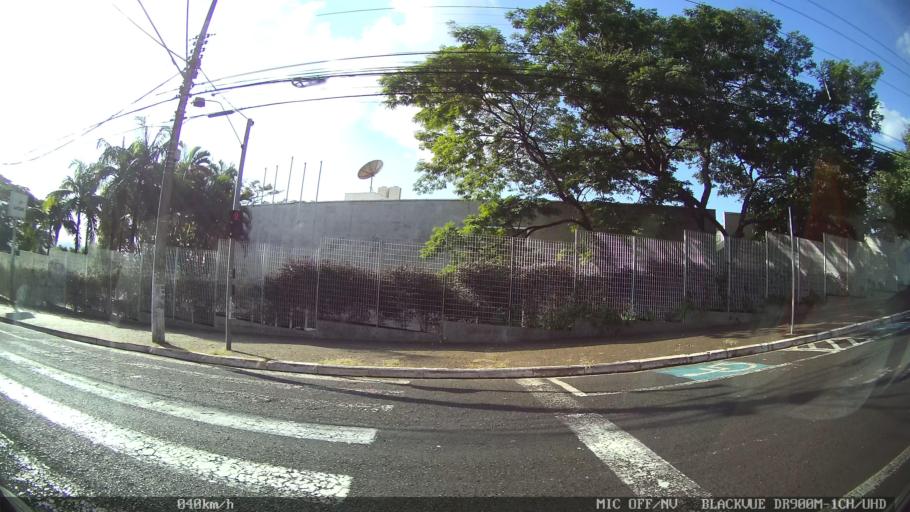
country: BR
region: Sao Paulo
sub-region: Ribeirao Preto
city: Ribeirao Preto
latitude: -21.1716
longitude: -47.7982
